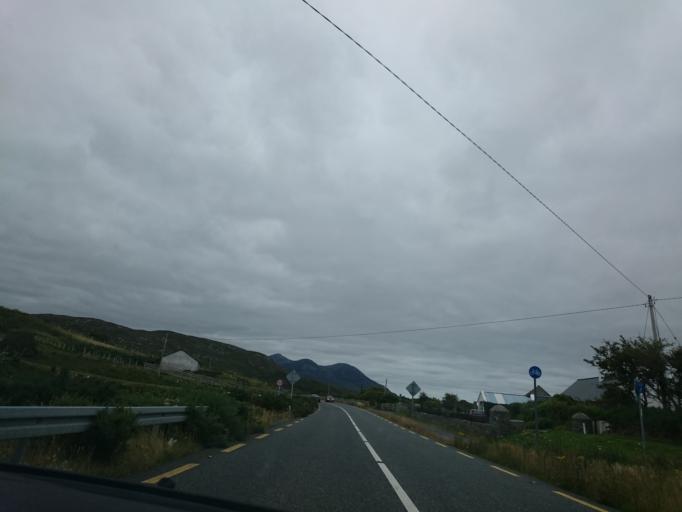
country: IE
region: Connaught
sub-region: County Galway
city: Clifden
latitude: 53.4820
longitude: -9.9645
